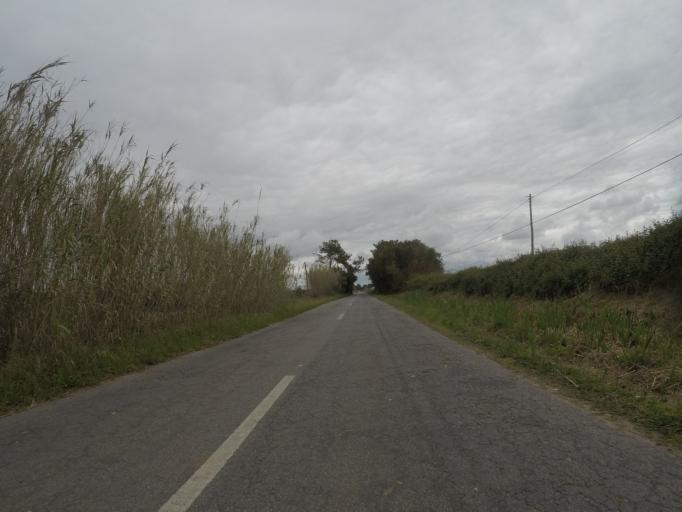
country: PT
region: Beja
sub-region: Odemira
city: Vila Nova de Milfontes
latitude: 37.6026
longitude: -8.8024
